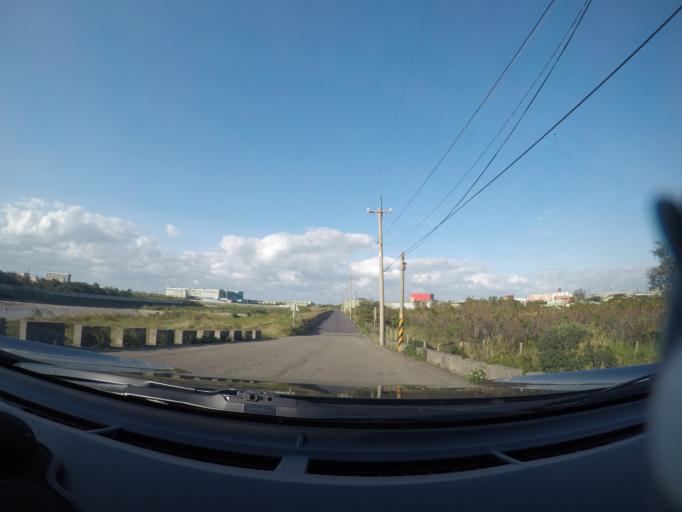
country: TW
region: Taiwan
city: Taoyuan City
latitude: 25.1019
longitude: 121.2518
